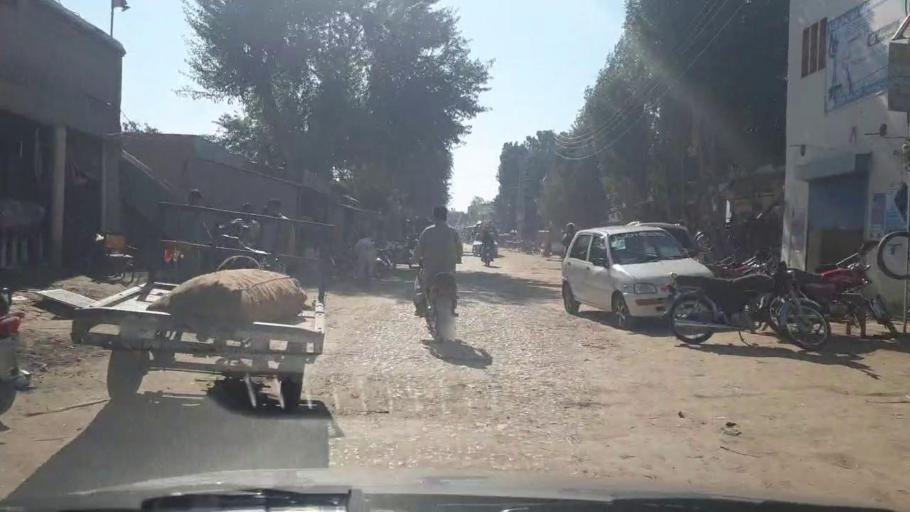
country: PK
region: Sindh
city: Bozdar
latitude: 27.1848
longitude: 68.6386
